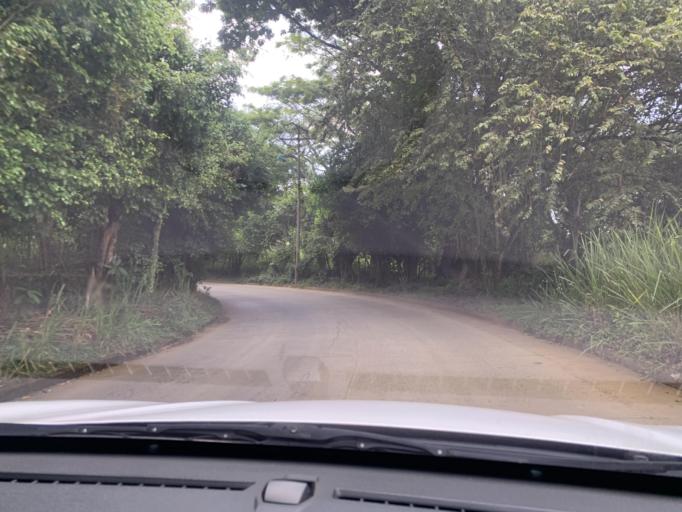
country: CO
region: Valle del Cauca
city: Jamundi
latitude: 3.3353
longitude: -76.5501
